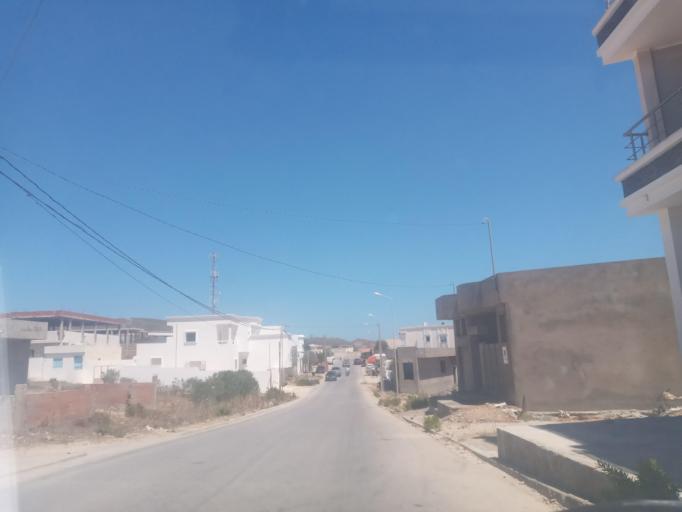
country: TN
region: Nabul
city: El Haouaria
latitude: 37.0559
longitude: 11.0001
